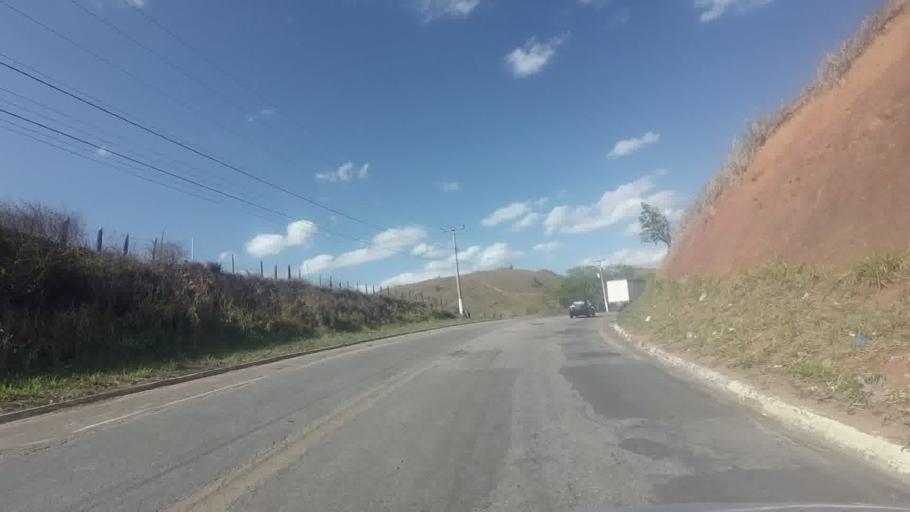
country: BR
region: Rio de Janeiro
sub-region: Bom Jesus Do Itabapoana
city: Bom Jesus do Itabapoana
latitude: -21.1307
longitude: -41.6592
